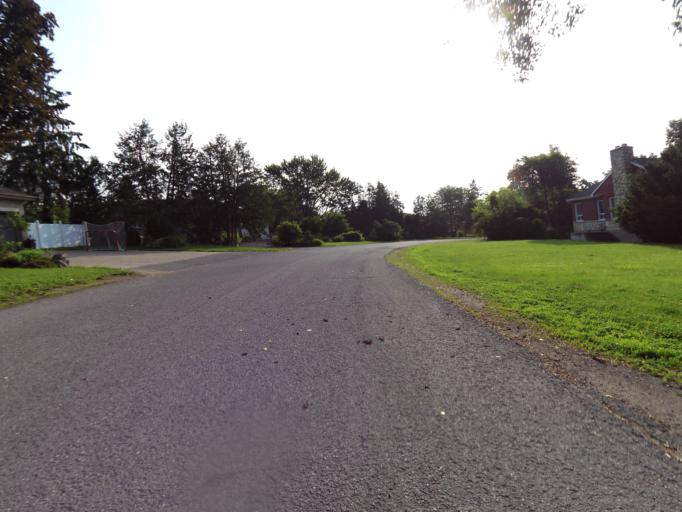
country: CA
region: Ontario
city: Ottawa
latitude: 45.3514
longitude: -75.7371
